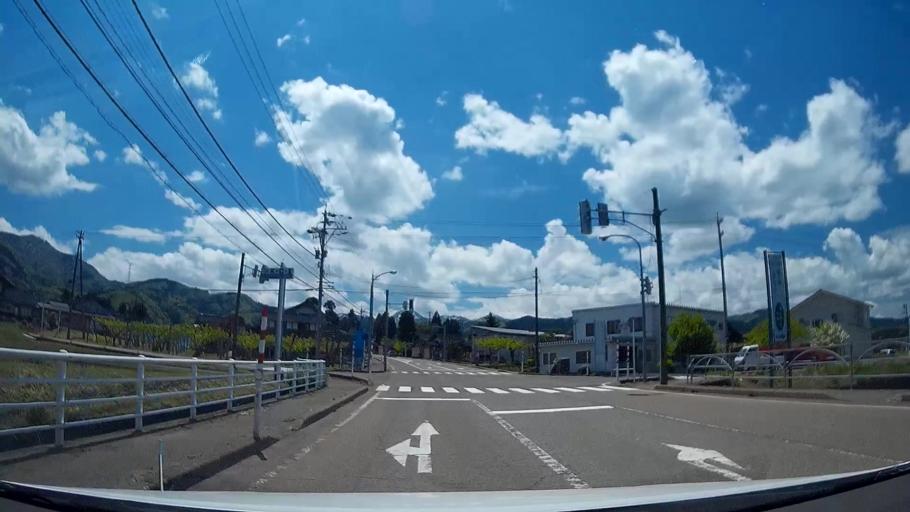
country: JP
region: Toyama
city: Fukumitsu
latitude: 36.4993
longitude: 136.8965
